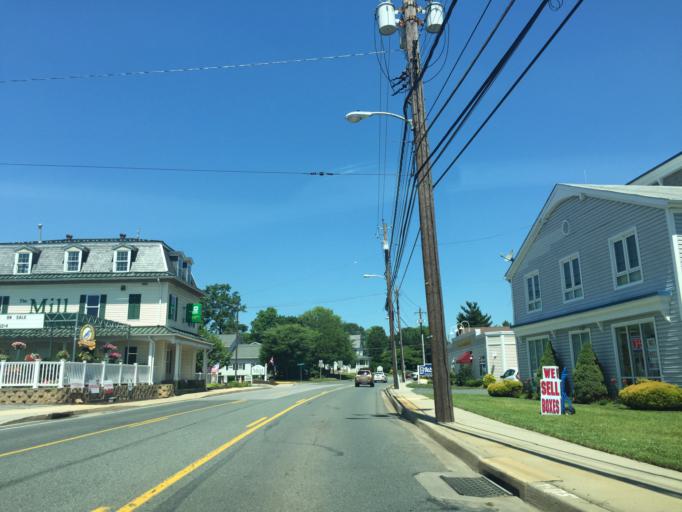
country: US
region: Maryland
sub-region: Harford County
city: North Bel Air
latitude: 39.5401
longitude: -76.3565
